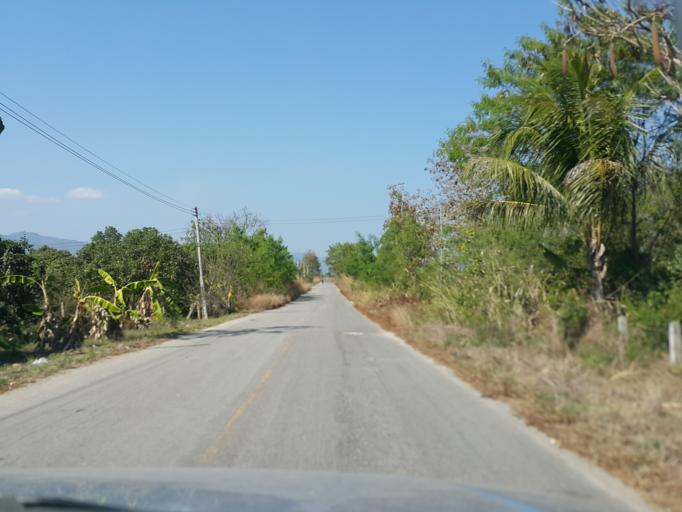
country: TH
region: Chiang Mai
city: Mae Wang
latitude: 18.5653
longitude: 98.7921
